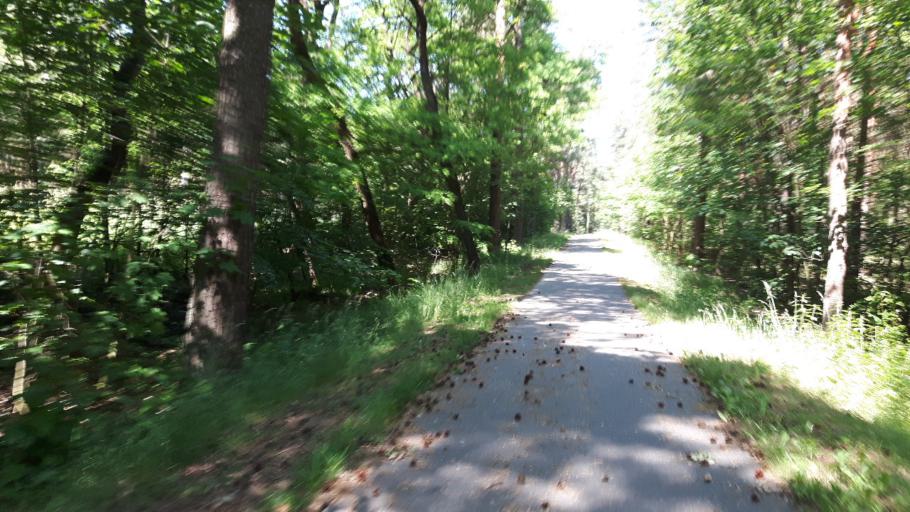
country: DE
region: Brandenburg
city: Treuenbrietzen
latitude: 52.0533
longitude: 12.8197
